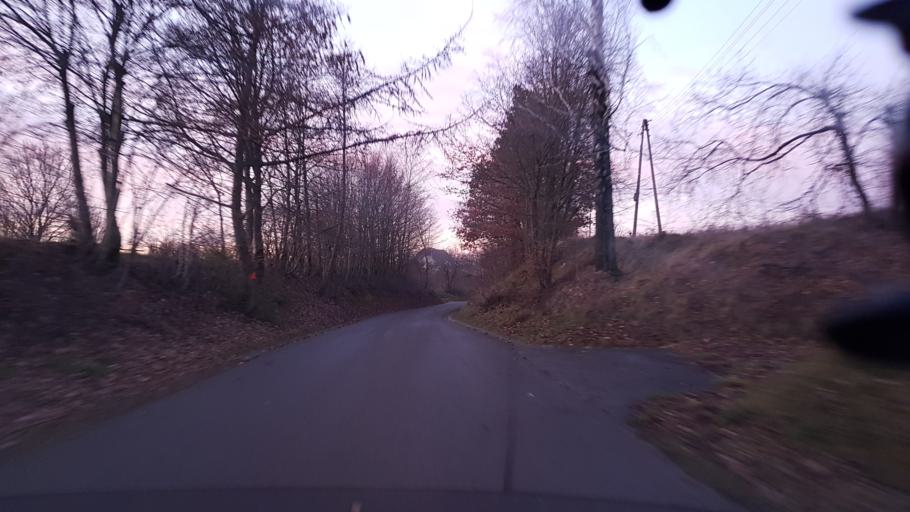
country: PL
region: Pomeranian Voivodeship
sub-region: Powiat bytowski
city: Tuchomie
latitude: 54.1307
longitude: 17.3670
